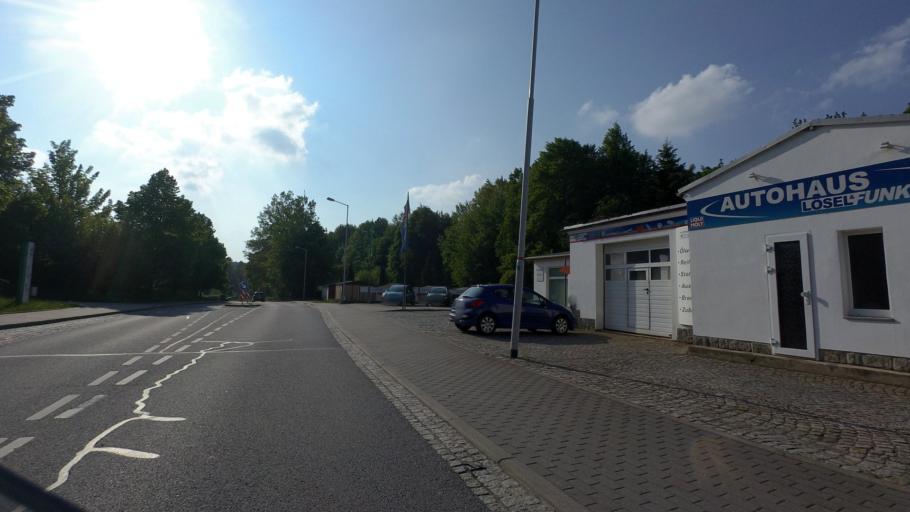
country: DE
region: Saxony
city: Sebnitz
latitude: 50.9837
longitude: 14.2672
